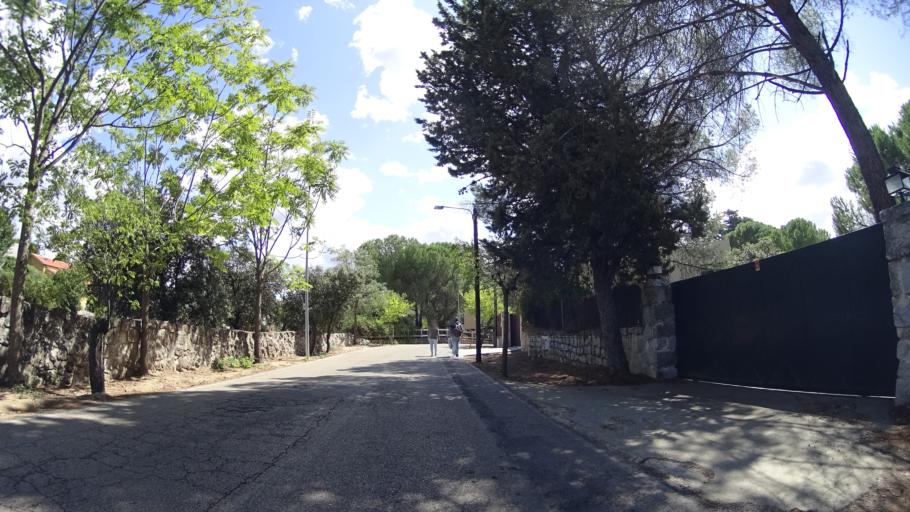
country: ES
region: Madrid
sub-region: Provincia de Madrid
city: Torrelodones
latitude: 40.5711
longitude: -3.9523
